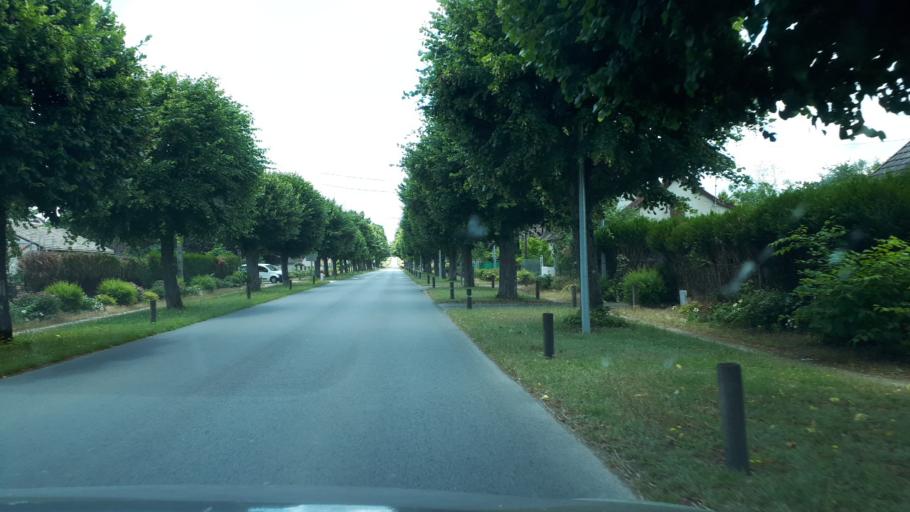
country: FR
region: Centre
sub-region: Departement du Loir-et-Cher
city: Contres
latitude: 47.4112
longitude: 1.4239
